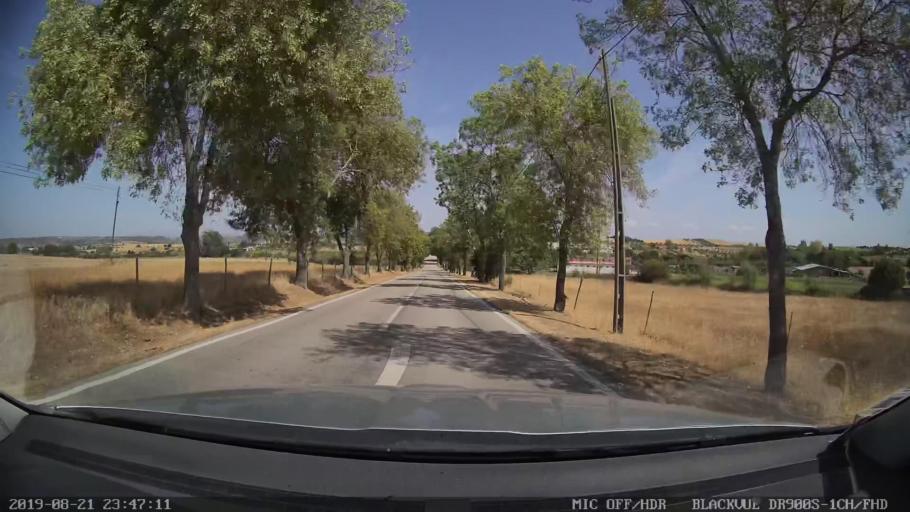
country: PT
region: Castelo Branco
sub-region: Idanha-A-Nova
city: Idanha-a-Nova
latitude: 39.8486
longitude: -7.2571
